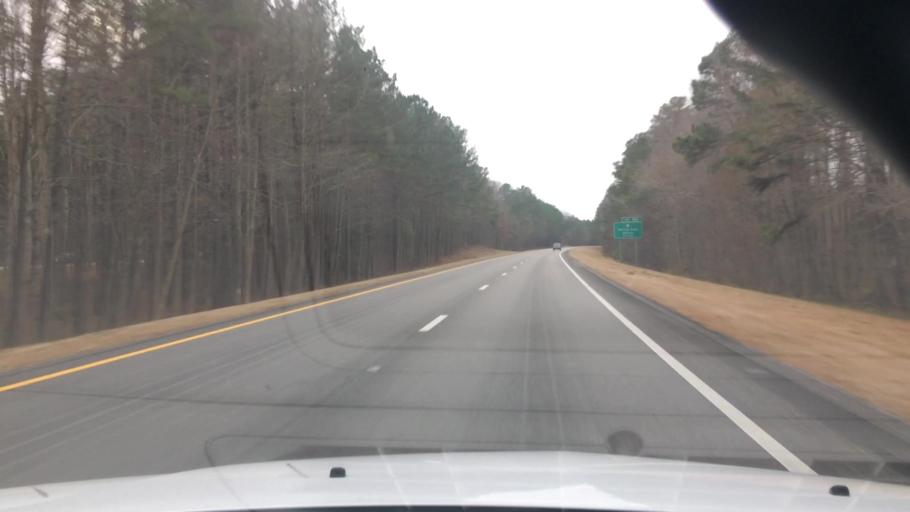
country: US
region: North Carolina
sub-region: Nash County
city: Spring Hope
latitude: 35.9325
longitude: -78.0742
